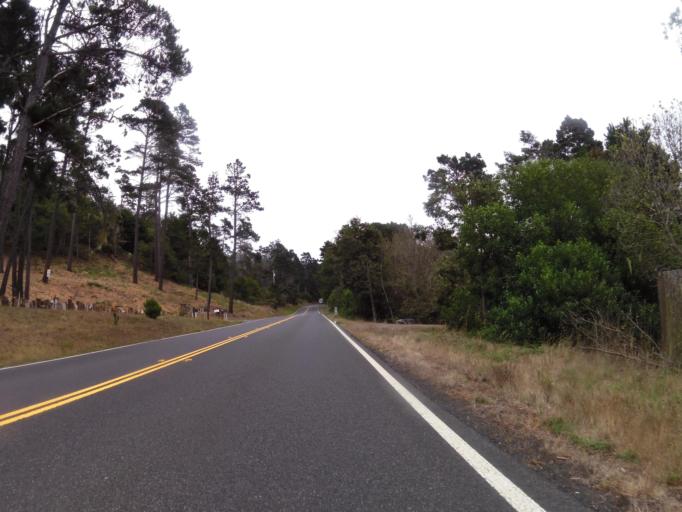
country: US
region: California
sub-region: Sonoma County
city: Sea Ranch
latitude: 38.5406
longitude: -123.2853
